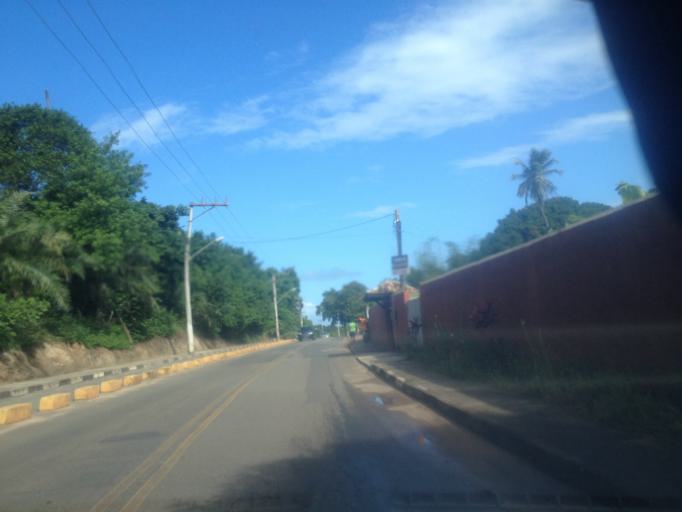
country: BR
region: Bahia
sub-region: Mata De Sao Joao
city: Mata de Sao Joao
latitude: -12.5983
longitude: -38.0408
